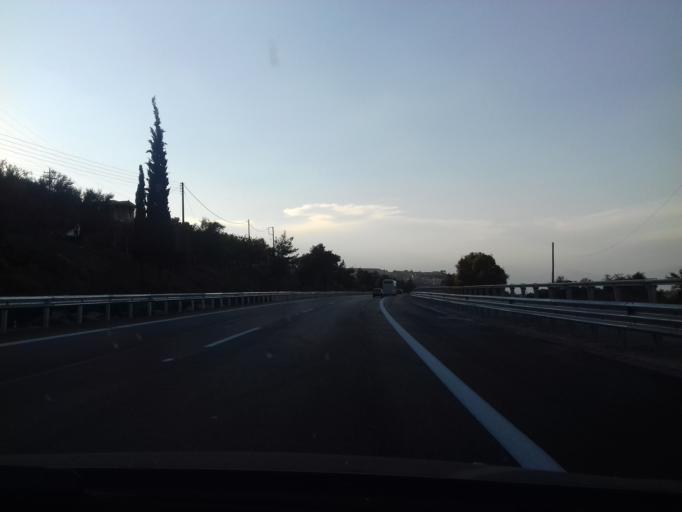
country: GR
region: West Greece
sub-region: Nomos Achaias
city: Aiyira
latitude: 38.1502
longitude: 22.3491
